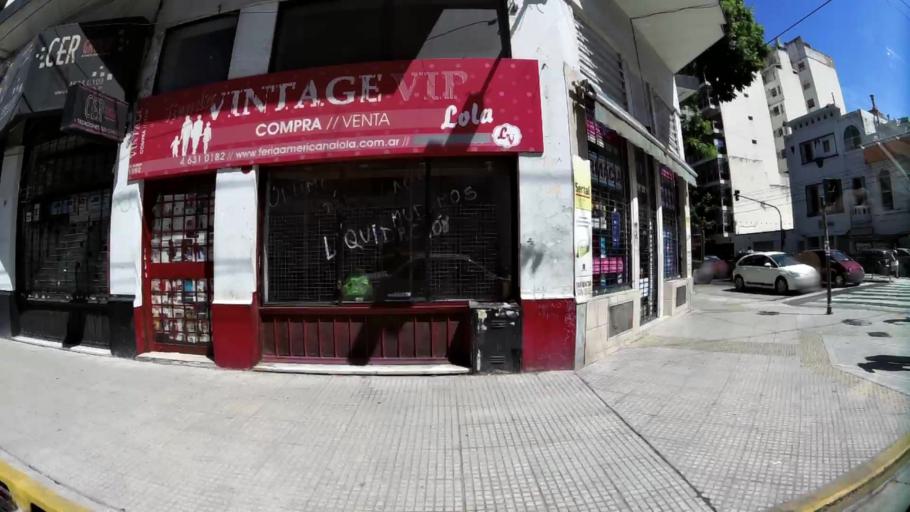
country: AR
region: Buenos Aires F.D.
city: Villa Santa Rita
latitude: -34.6293
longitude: -58.4553
